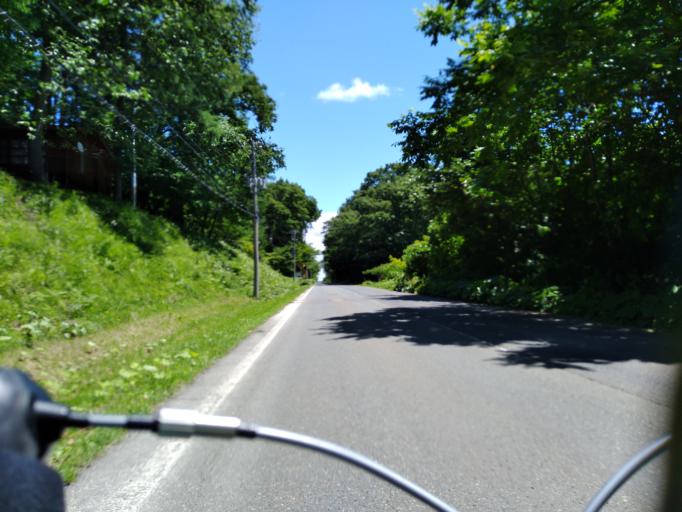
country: JP
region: Iwate
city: Shizukuishi
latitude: 39.7609
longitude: 140.9698
